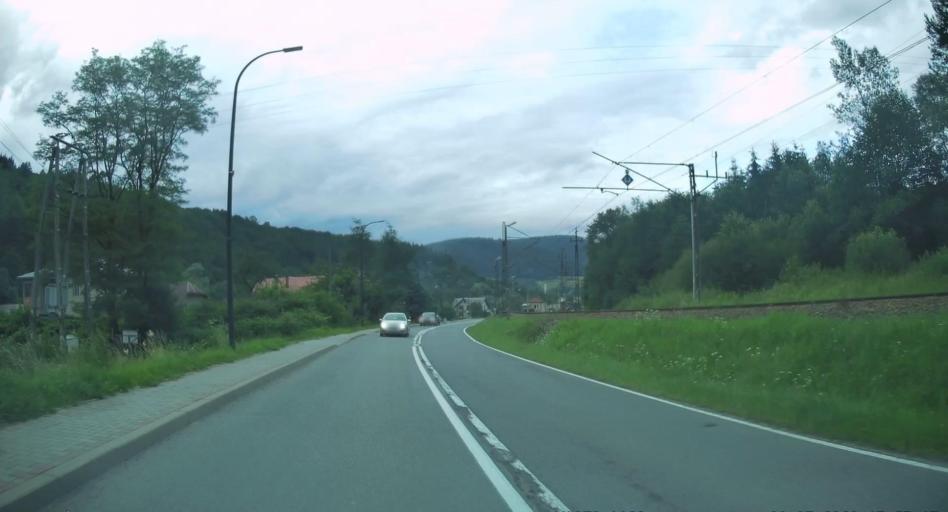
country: PL
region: Lesser Poland Voivodeship
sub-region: Powiat nowosadecki
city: Piwniczna-Zdroj
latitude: 49.3643
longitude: 20.7826
